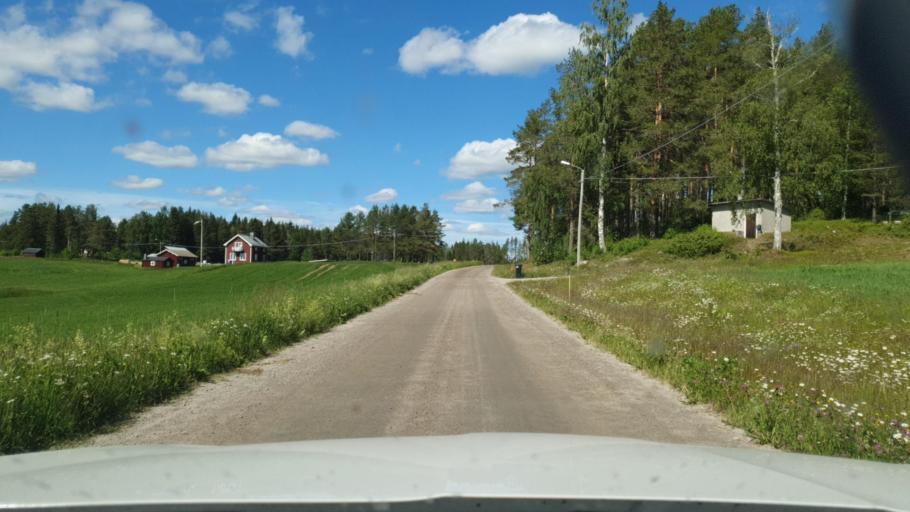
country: SE
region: Vaesterbotten
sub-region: Skelleftea Kommun
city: Byske
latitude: 65.1217
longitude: 21.2079
